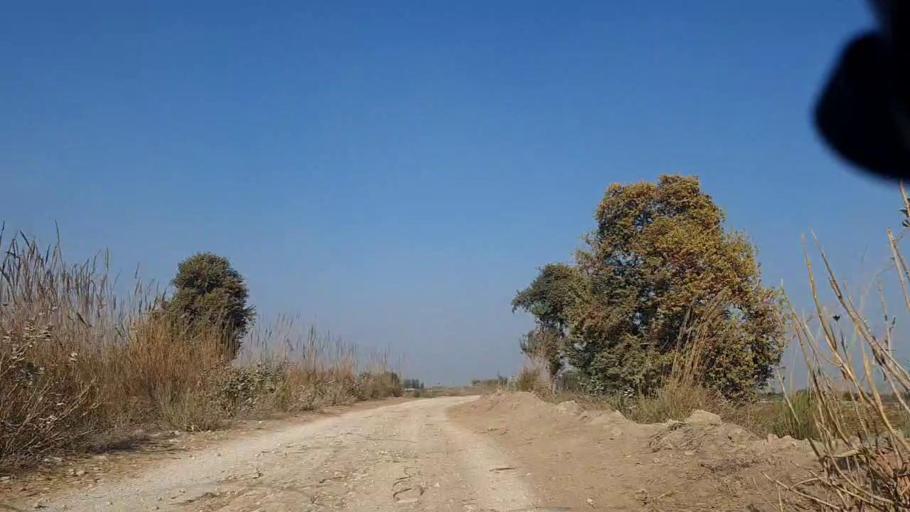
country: PK
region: Sindh
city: Khanpur
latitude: 27.6917
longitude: 69.4975
